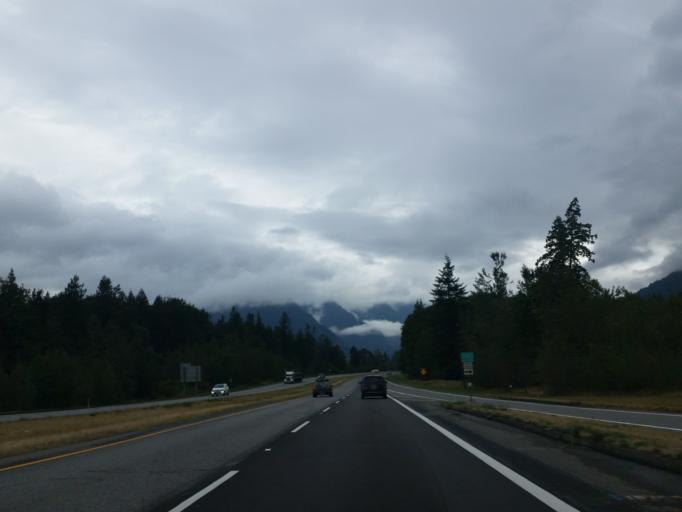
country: CA
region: British Columbia
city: Agassiz
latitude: 49.3125
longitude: -121.6332
